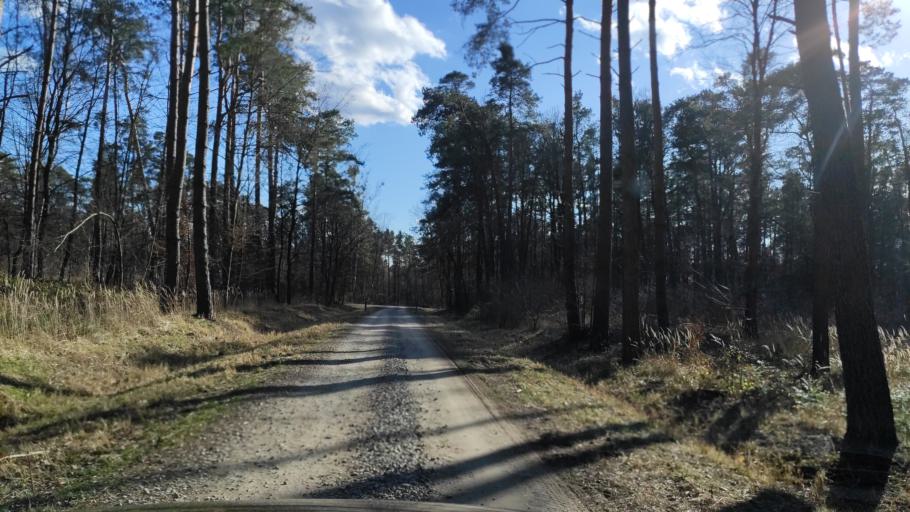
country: PL
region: Masovian Voivodeship
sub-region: Powiat radomski
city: Jedlnia-Letnisko
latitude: 51.4444
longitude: 21.2933
